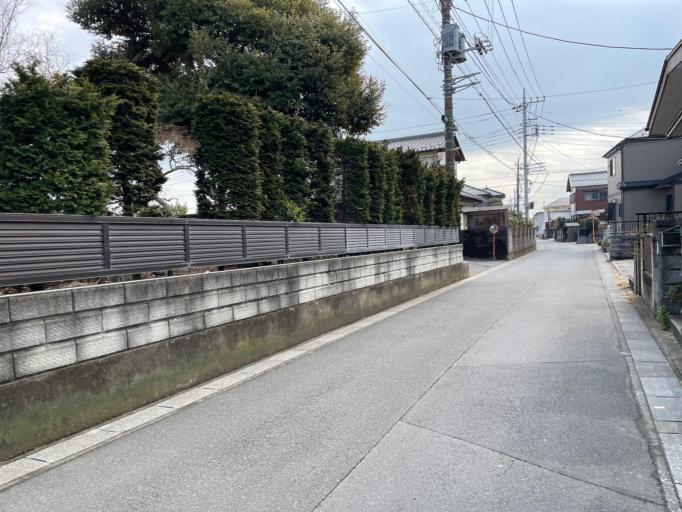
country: JP
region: Saitama
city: Yashio-shi
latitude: 35.8399
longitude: 139.8480
